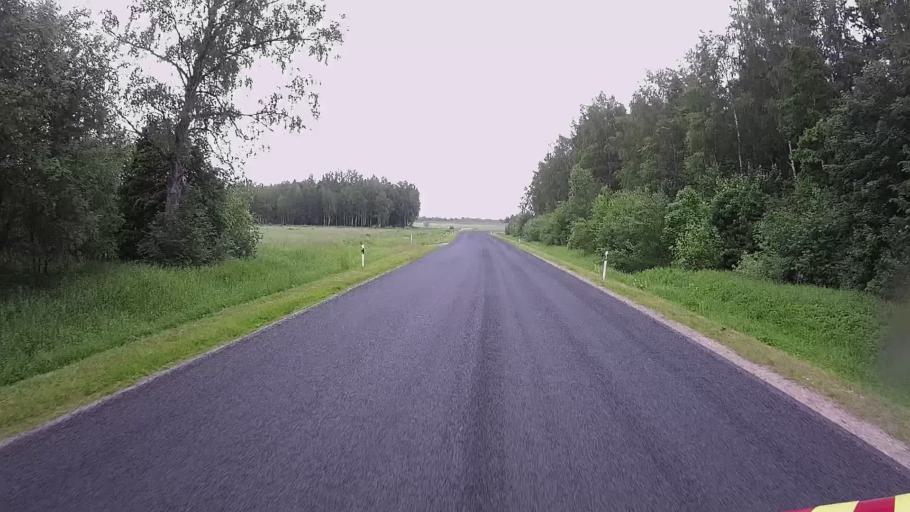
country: EE
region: Jogevamaa
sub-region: Poltsamaa linn
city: Poltsamaa
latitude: 58.5361
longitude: 25.9501
